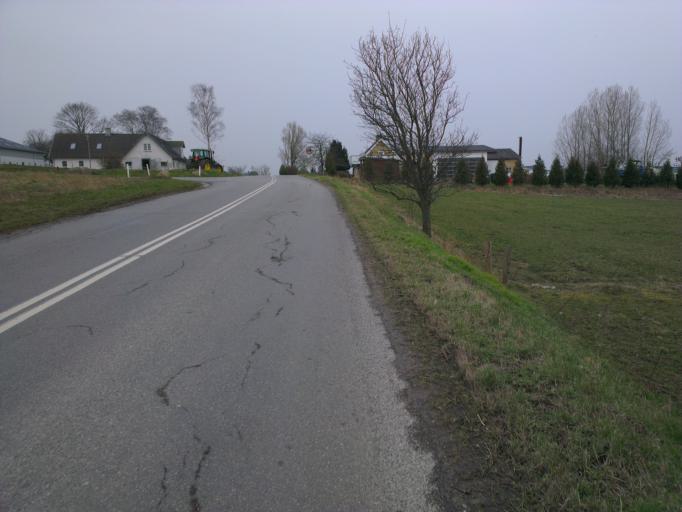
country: DK
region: Capital Region
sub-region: Frederikssund Kommune
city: Skibby
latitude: 55.7421
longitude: 11.9274
